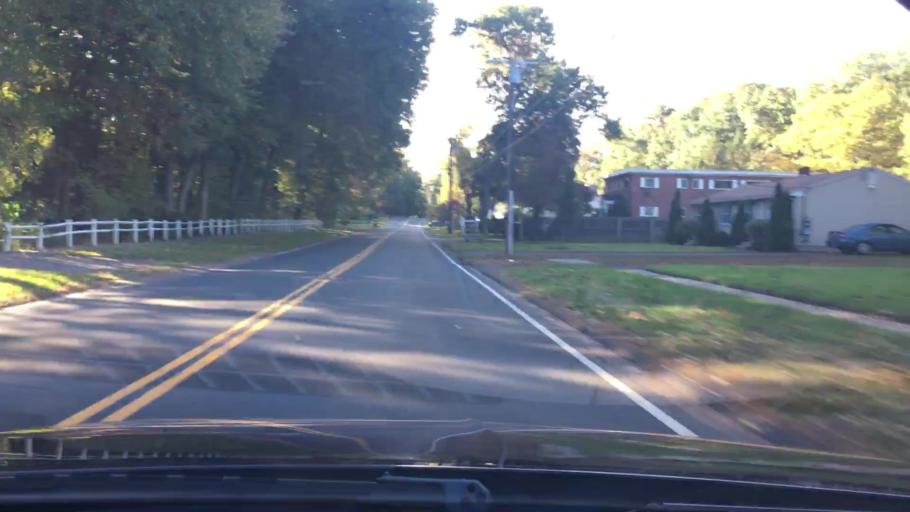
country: US
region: Connecticut
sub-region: Hartford County
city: Sherwood Manor
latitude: 42.0280
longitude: -72.5602
